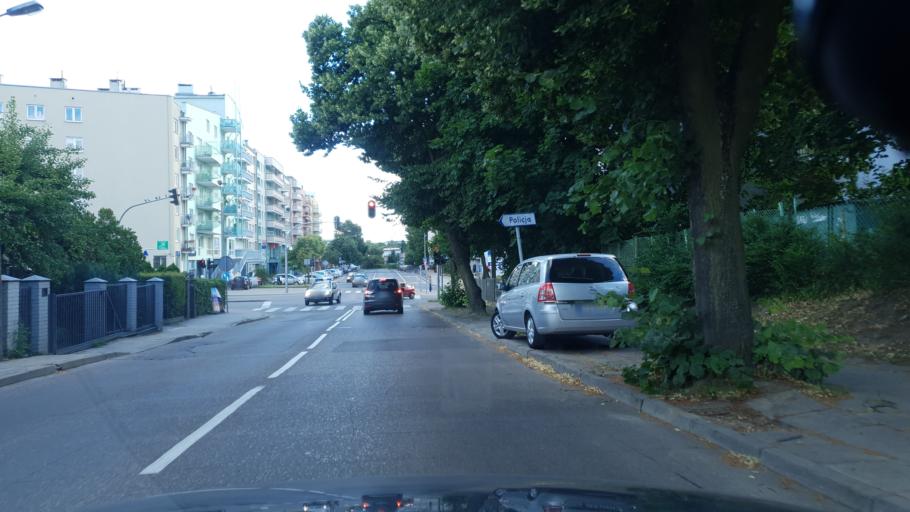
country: PL
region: Pomeranian Voivodeship
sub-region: Gdynia
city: Gdynia
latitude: 54.4979
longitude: 18.5417
